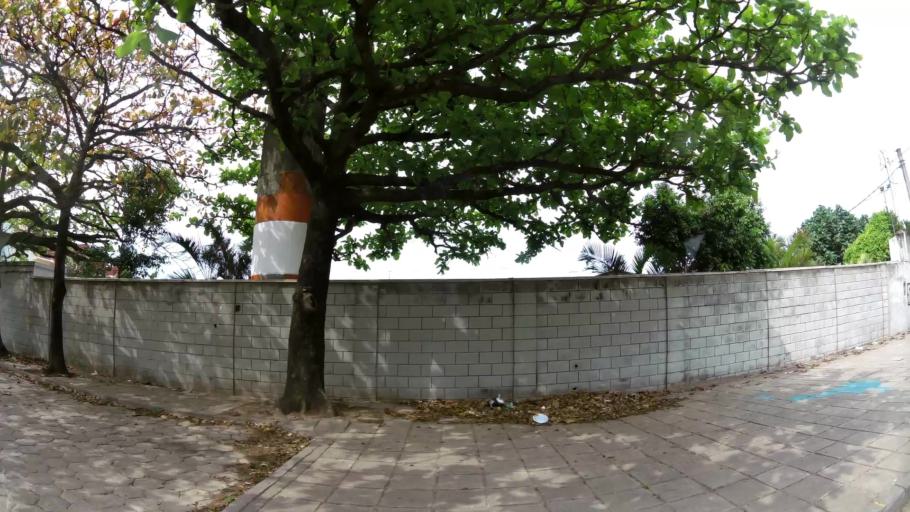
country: BO
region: Santa Cruz
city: Santa Cruz de la Sierra
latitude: -17.7792
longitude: -63.2105
